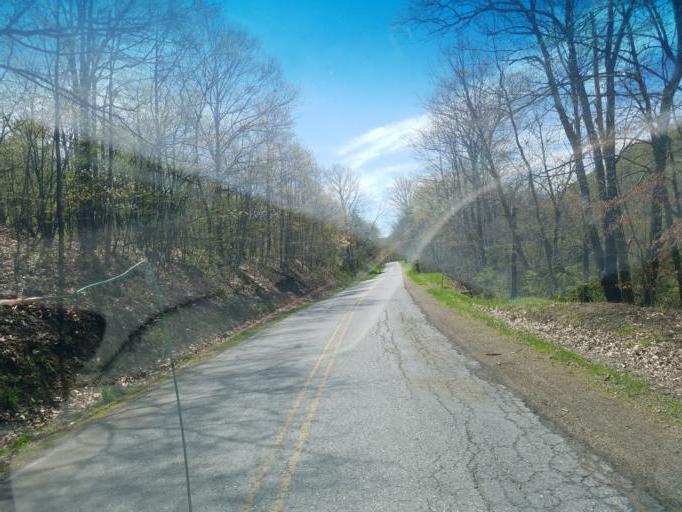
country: US
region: Pennsylvania
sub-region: Potter County
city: Galeton
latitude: 41.8643
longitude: -77.7170
